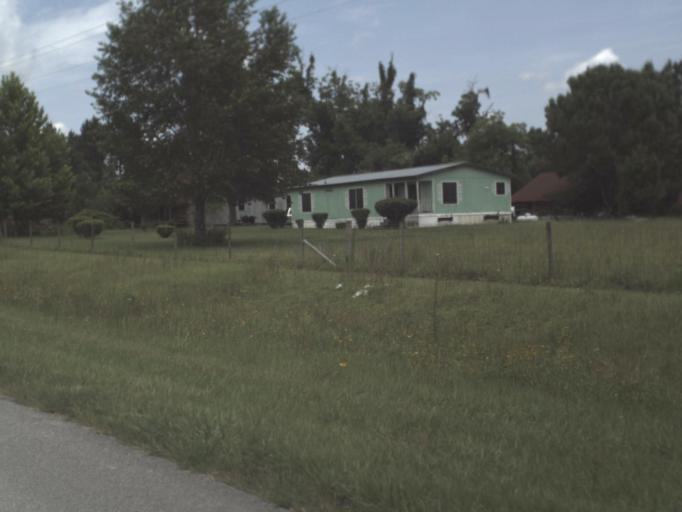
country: US
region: Florida
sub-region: Madison County
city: Madison
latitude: 30.5640
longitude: -83.4296
